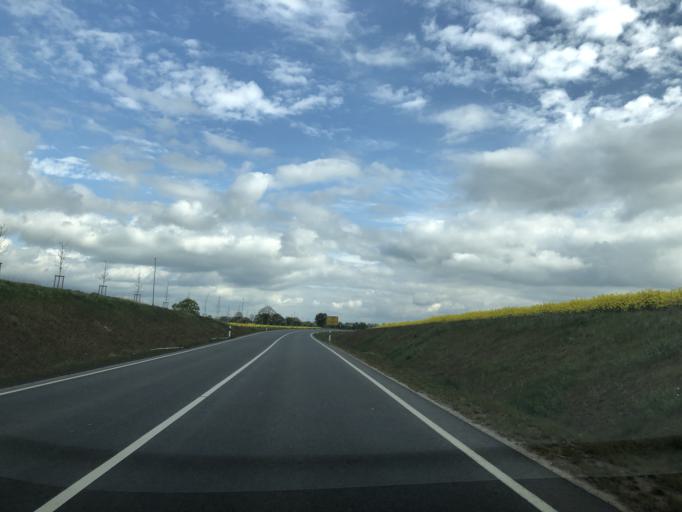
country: DE
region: Mecklenburg-Vorpommern
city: Plau am See
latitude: 53.4646
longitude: 12.2493
